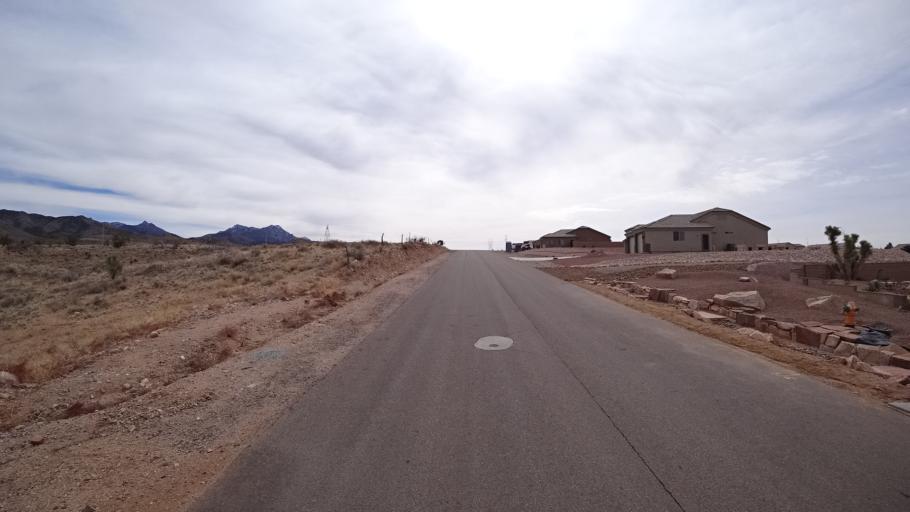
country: US
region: Arizona
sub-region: Mohave County
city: Kingman
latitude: 35.1841
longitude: -113.9763
